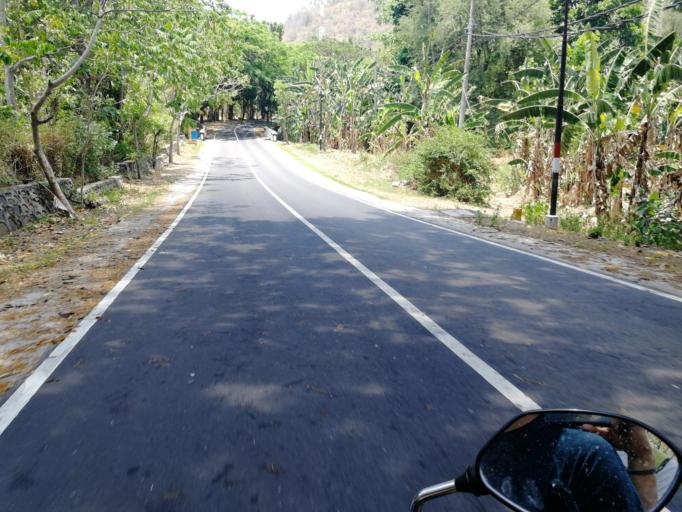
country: ID
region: West Nusa Tenggara
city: Karangsubagan
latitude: -8.4444
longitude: 116.0412
